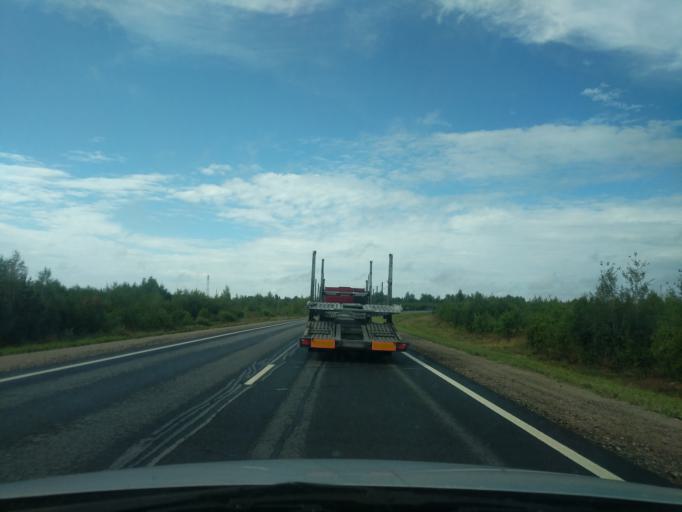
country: RU
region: Kostroma
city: Sudislavl'
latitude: 57.8216
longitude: 41.9066
